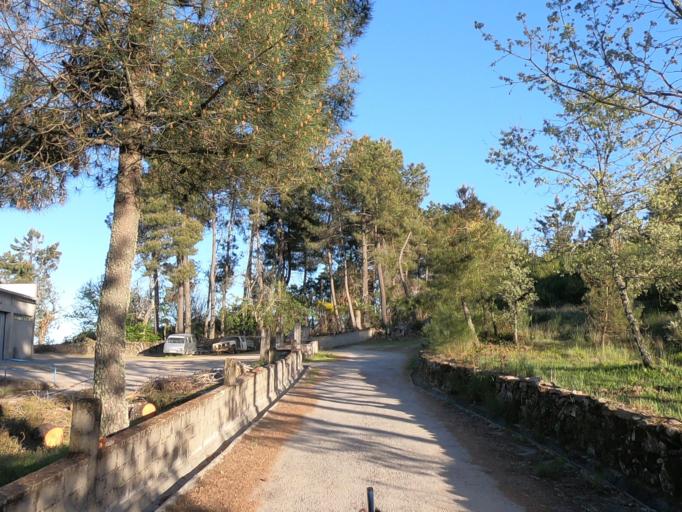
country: PT
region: Vila Real
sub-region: Sabrosa
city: Sabrosa
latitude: 41.3558
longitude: -7.6215
